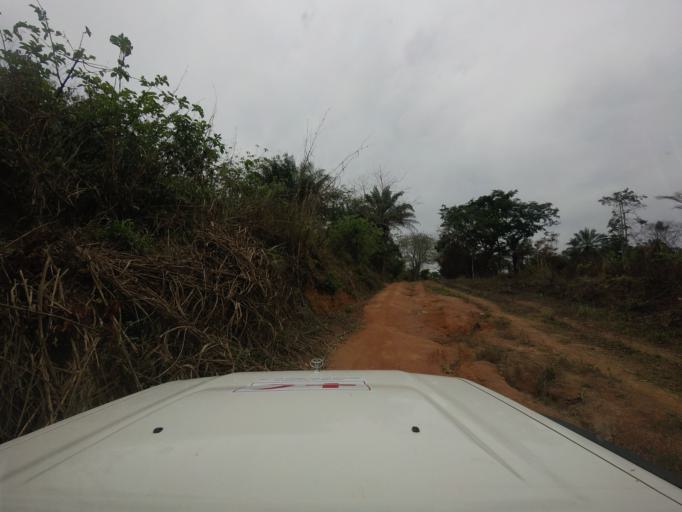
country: SL
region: Eastern Province
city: Buedu
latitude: 8.2734
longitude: -10.2847
